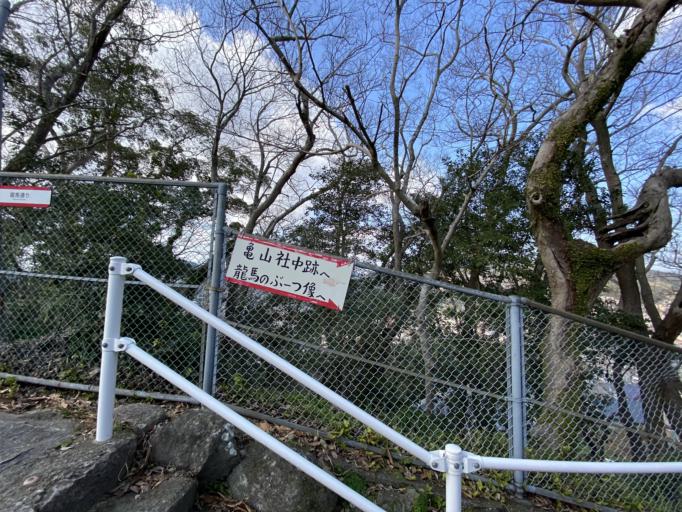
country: JP
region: Nagasaki
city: Nagasaki-shi
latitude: 32.7471
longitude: 129.8862
